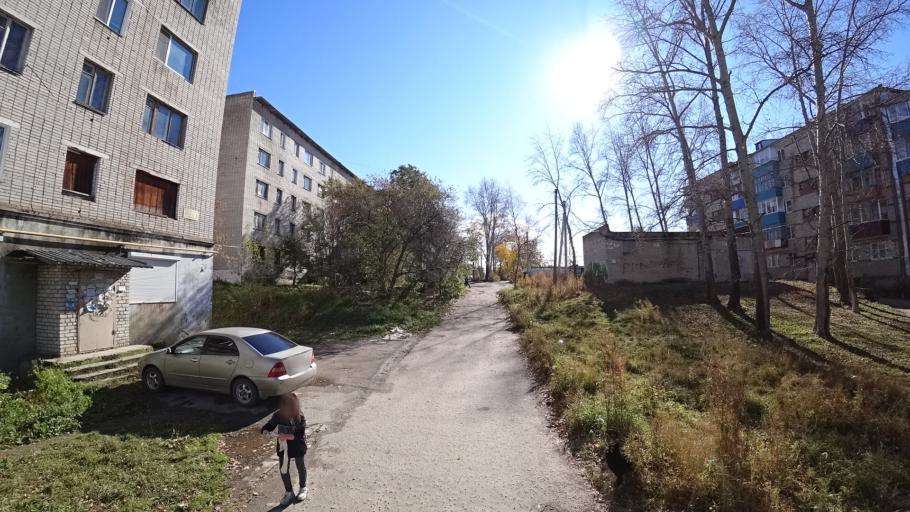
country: RU
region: Khabarovsk Krai
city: Amursk
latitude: 50.2209
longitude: 136.9022
